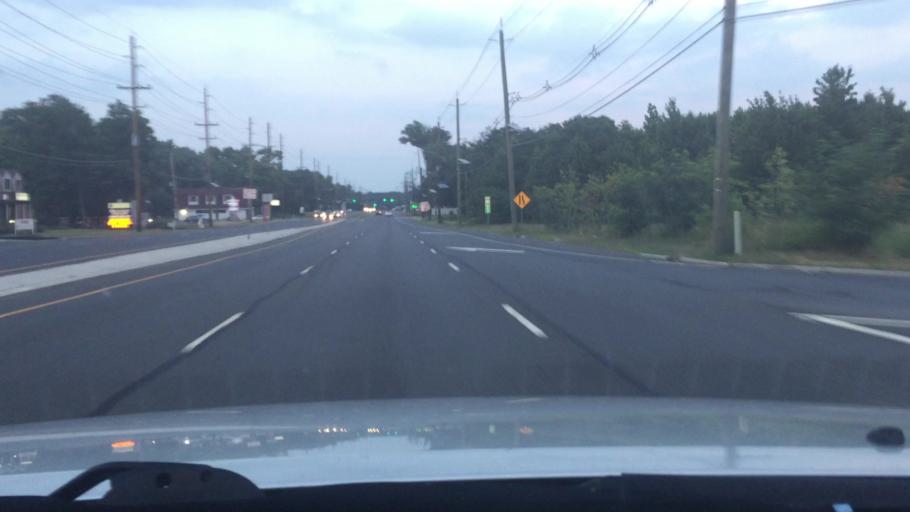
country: US
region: New Jersey
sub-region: Middlesex County
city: Milltown
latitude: 40.4410
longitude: -74.4761
